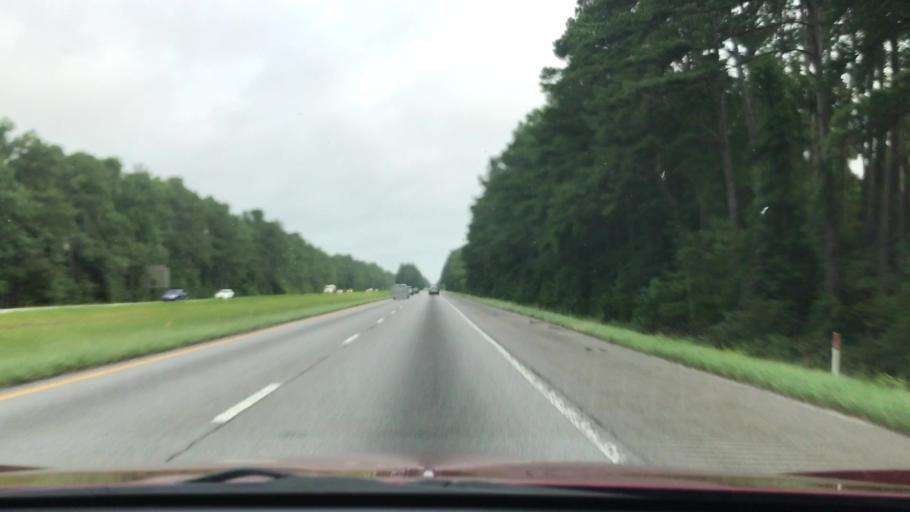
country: US
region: South Carolina
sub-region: Orangeburg County
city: Holly Hill
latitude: 33.2972
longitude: -80.5272
